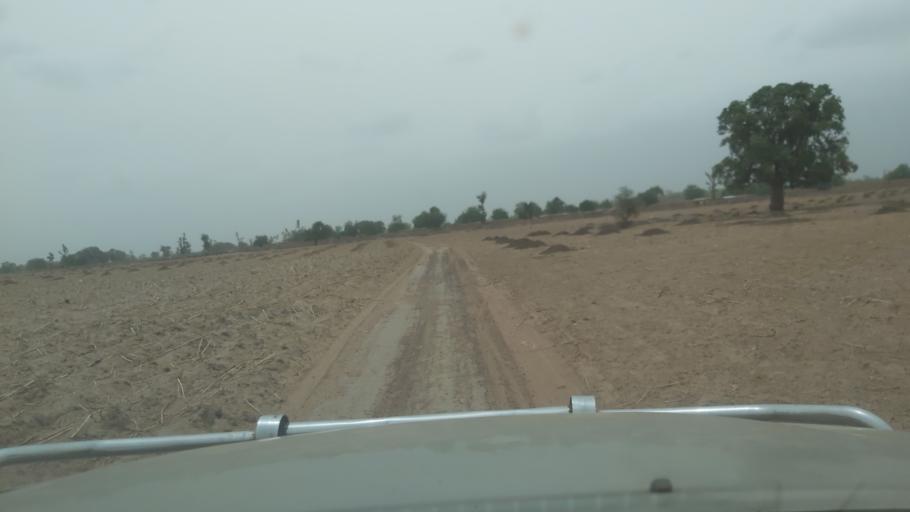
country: ML
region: Koulikoro
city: Banamba
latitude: 13.3763
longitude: -7.2266
